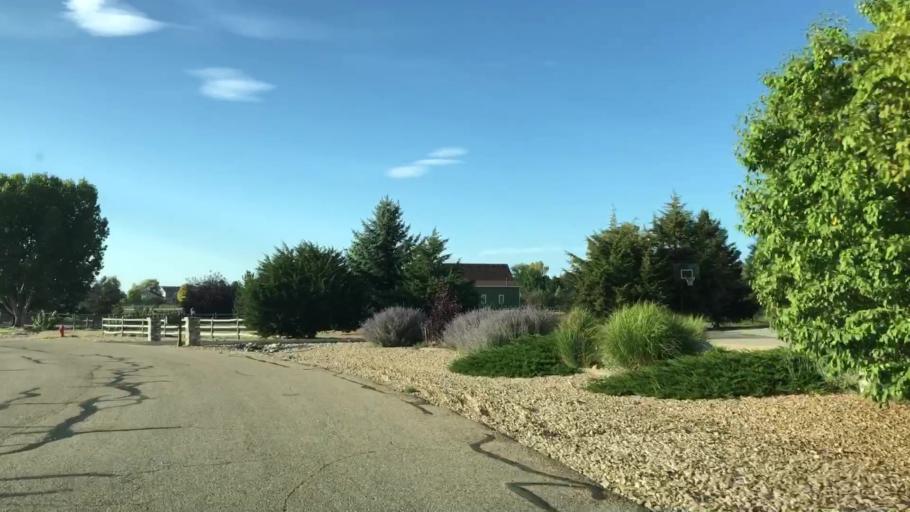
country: US
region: Colorado
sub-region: Weld County
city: Windsor
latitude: 40.4420
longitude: -104.9494
